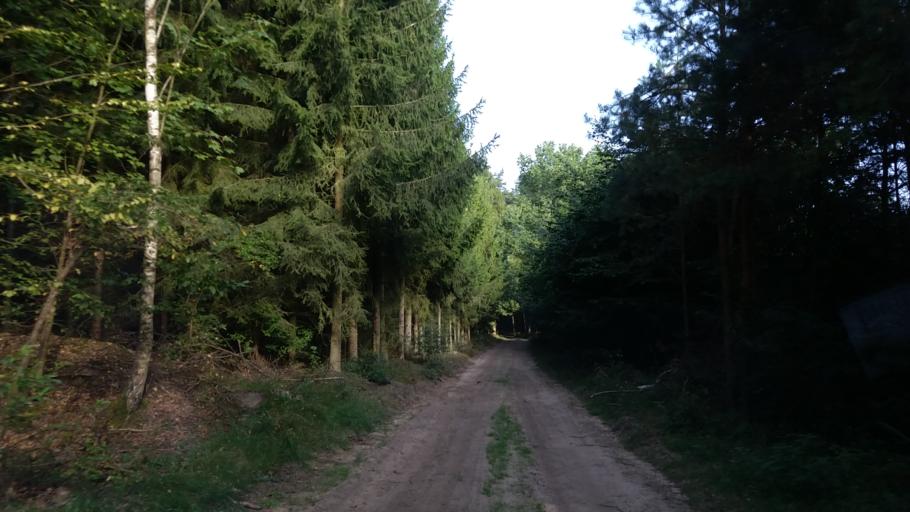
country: PL
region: West Pomeranian Voivodeship
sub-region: Powiat choszczenski
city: Choszczno
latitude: 53.2275
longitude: 15.4495
